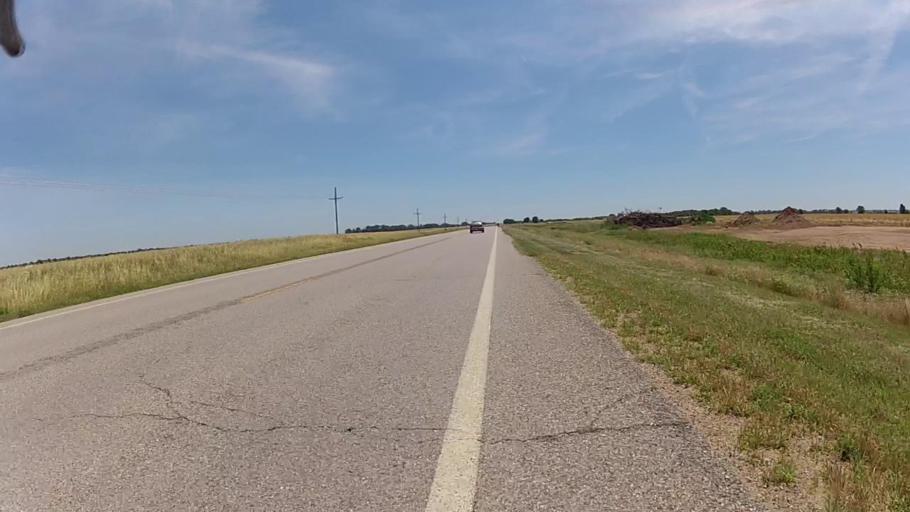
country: US
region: Kansas
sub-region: Barber County
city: Medicine Lodge
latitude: 37.2541
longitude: -98.5037
